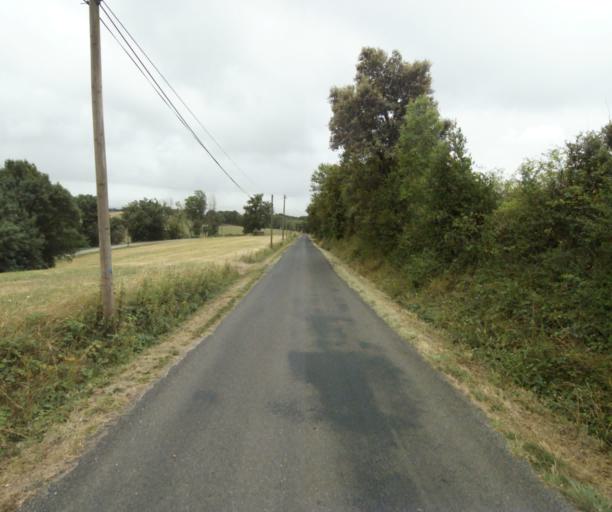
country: FR
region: Midi-Pyrenees
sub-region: Departement du Tarn
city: Soreze
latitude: 43.4015
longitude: 2.0618
